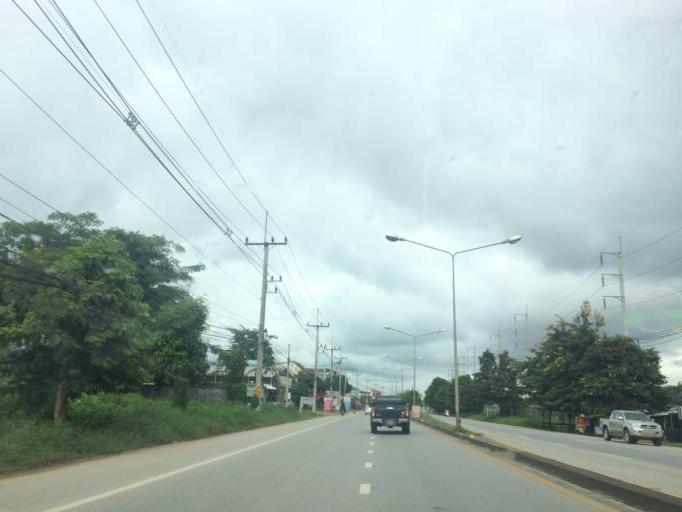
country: TH
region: Chiang Rai
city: Mae Chan
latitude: 20.0500
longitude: 99.8757
